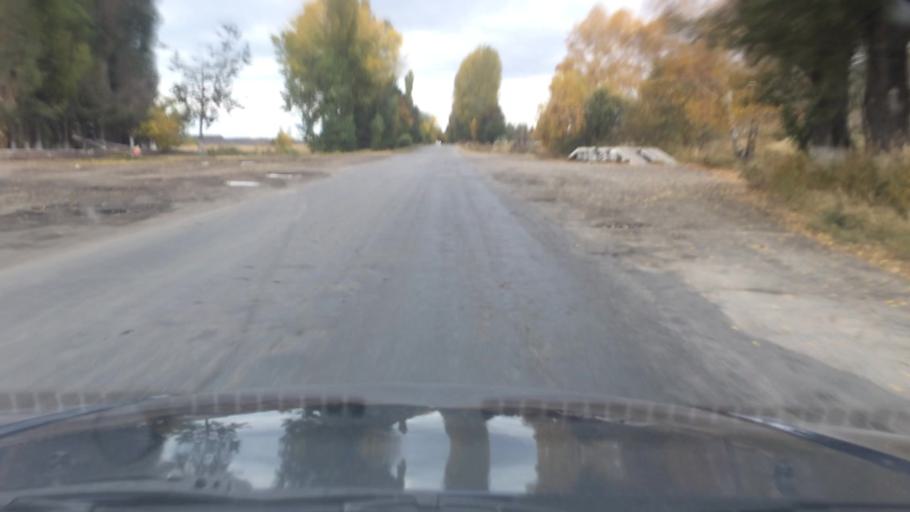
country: KG
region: Ysyk-Koel
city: Tyup
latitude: 42.7592
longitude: 78.1563
